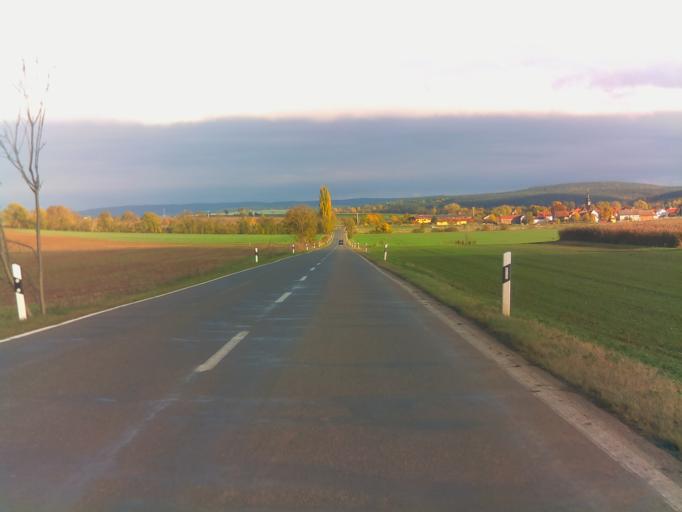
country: DE
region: Thuringia
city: Hohenfelden
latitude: 50.8816
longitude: 11.1449
